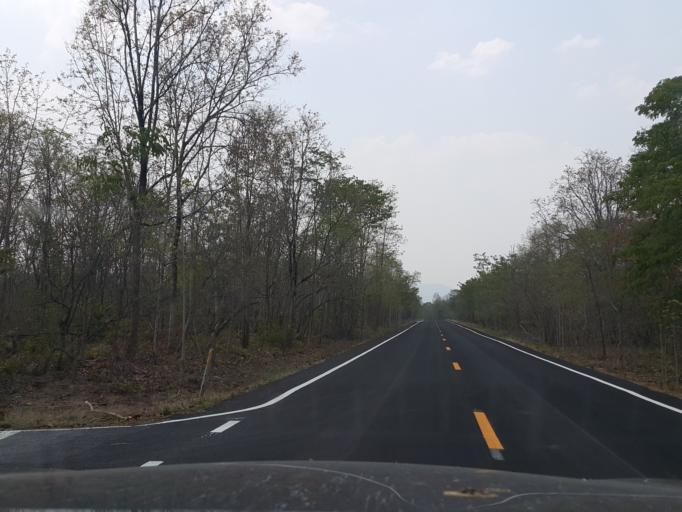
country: TH
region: Lampang
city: Mae Phrik
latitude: 17.4824
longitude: 99.1085
